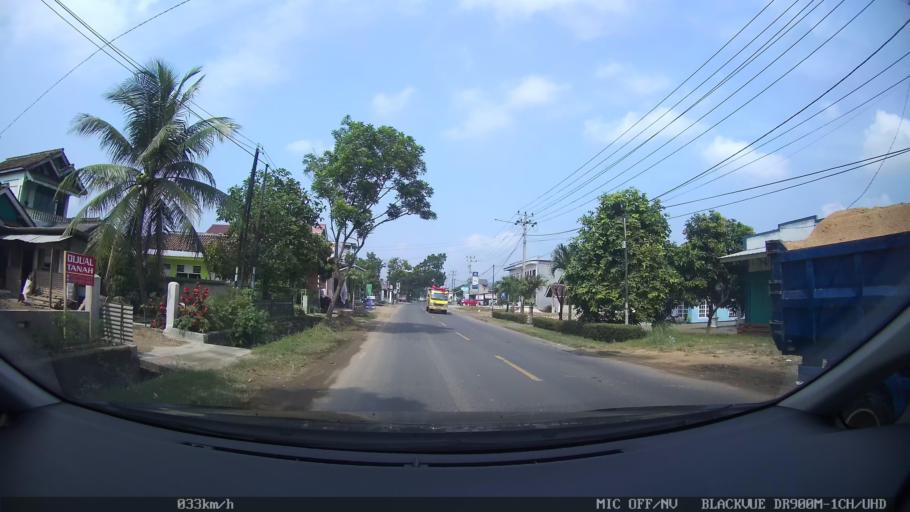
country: ID
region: Lampung
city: Gadingrejo
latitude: -5.3756
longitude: 105.0390
